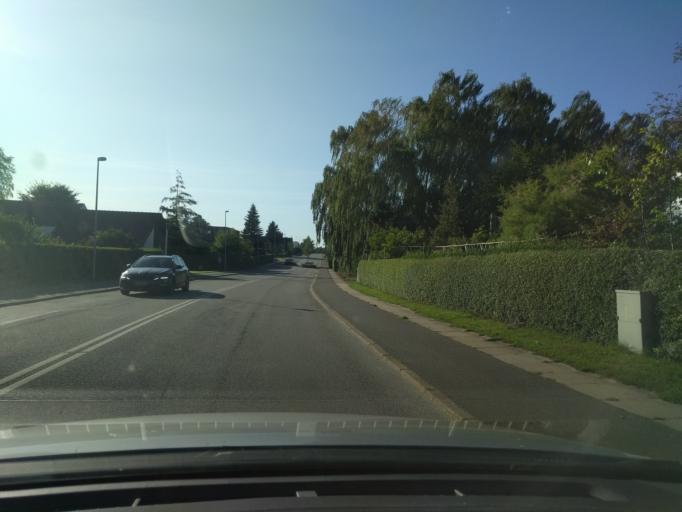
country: DK
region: Central Jutland
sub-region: Horsens Kommune
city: Horsens
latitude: 55.8644
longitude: 9.9096
